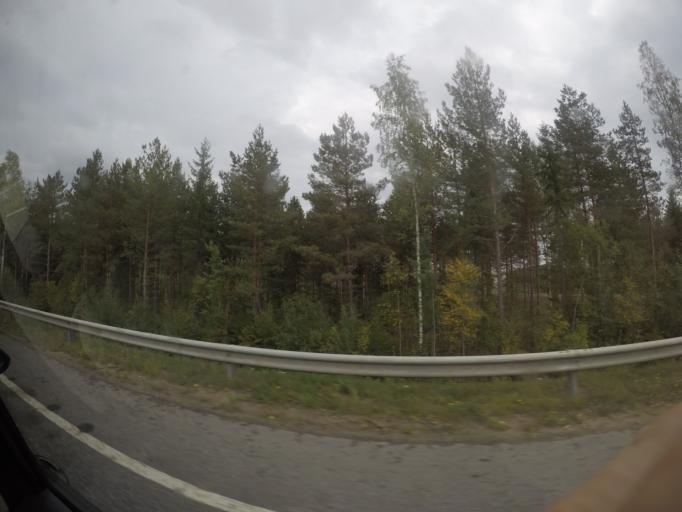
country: FI
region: Haeme
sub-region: Haemeenlinna
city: Parola
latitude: 61.1412
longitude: 24.4147
